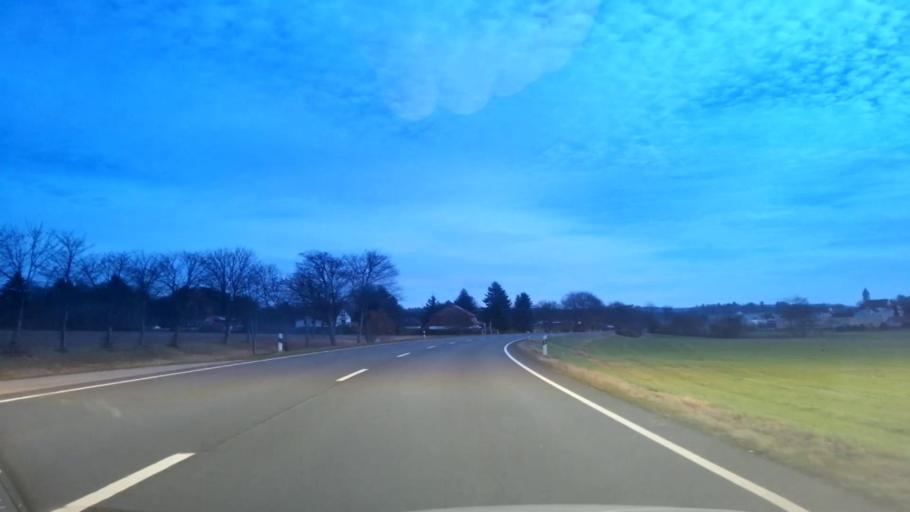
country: DE
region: Bavaria
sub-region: Upper Palatinate
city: Pechbrunn
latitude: 49.9749
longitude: 12.1570
